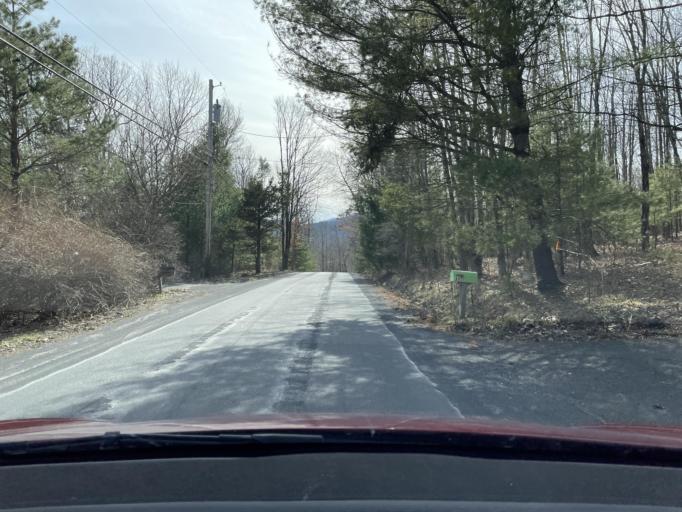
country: US
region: New York
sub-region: Ulster County
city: Woodstock
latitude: 42.0565
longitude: -74.1137
